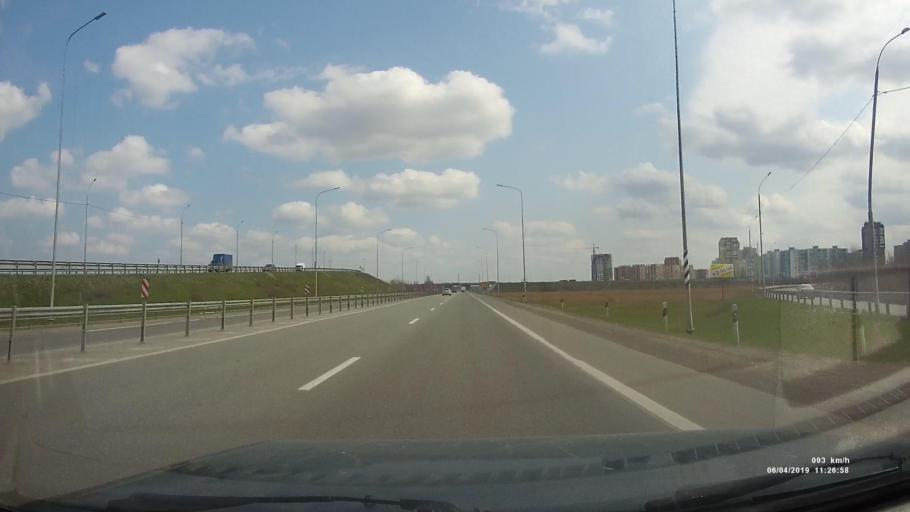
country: RU
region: Rostov
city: Bataysk
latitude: 47.1578
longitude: 39.7345
